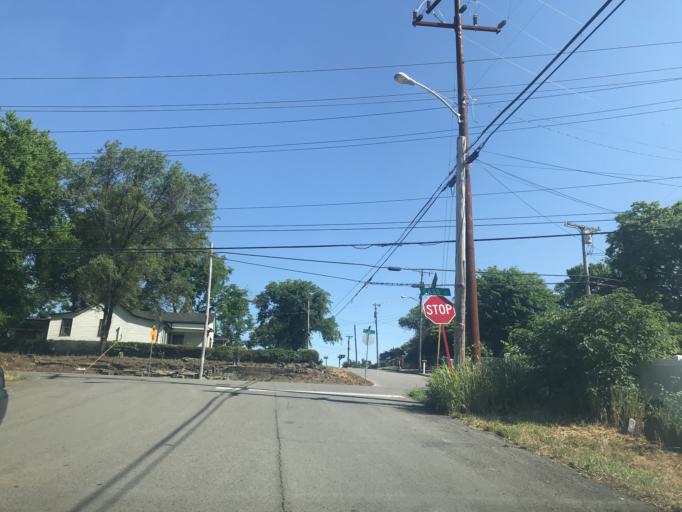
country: US
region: Tennessee
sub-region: Davidson County
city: Nashville
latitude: 36.1853
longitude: -86.8082
